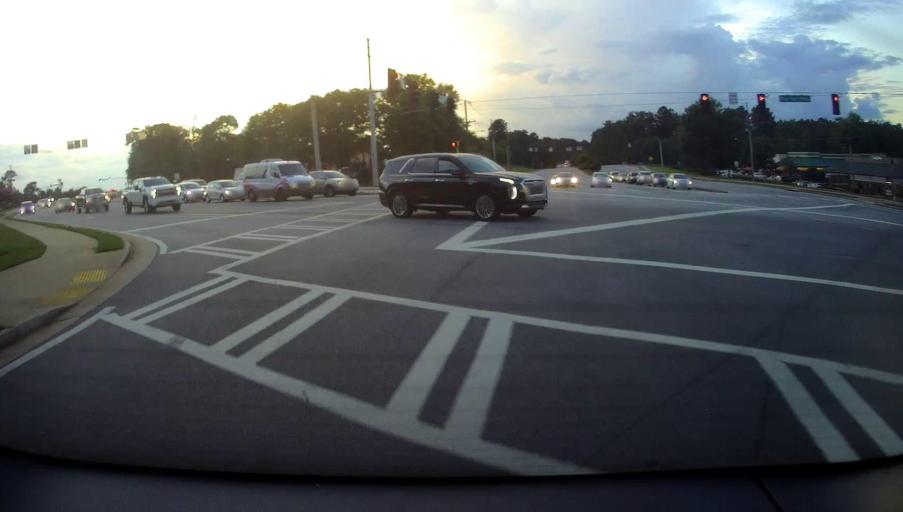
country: US
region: Georgia
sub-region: Fayette County
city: Peachtree City
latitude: 33.3972
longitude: -84.5910
